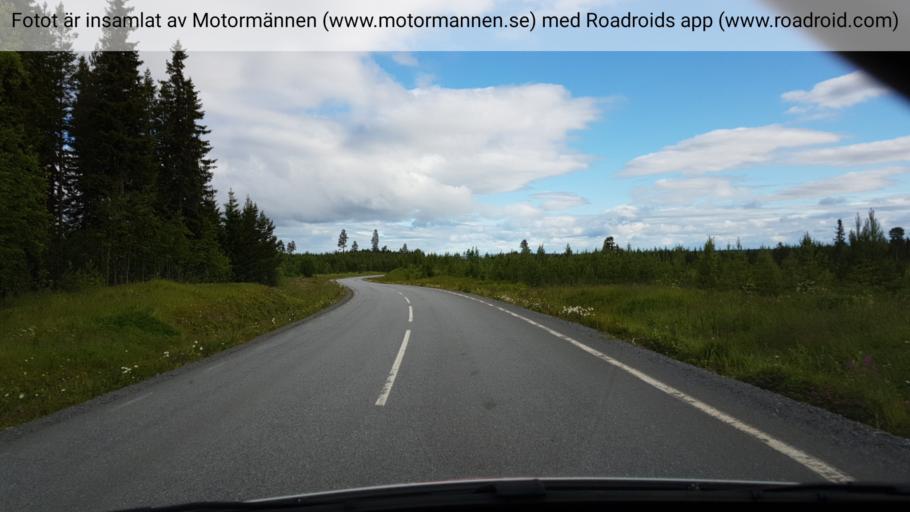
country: SE
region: Jaemtland
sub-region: Krokoms Kommun
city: Krokom
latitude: 63.2591
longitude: 14.4334
